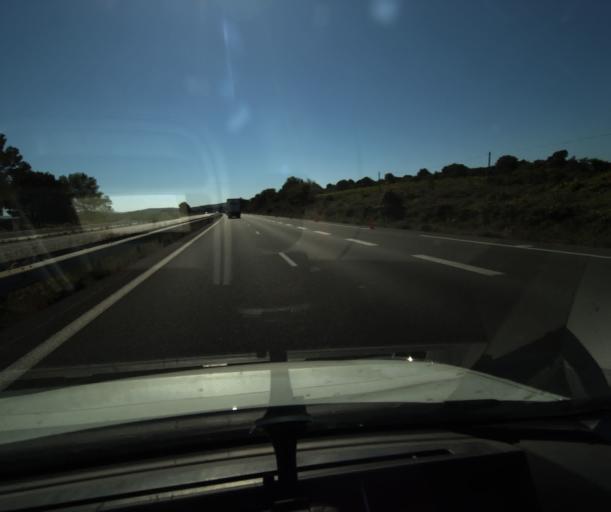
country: FR
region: Languedoc-Roussillon
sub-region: Departement de l'Aude
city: Ferrals-les-Corbieres
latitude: 43.1691
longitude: 2.7078
